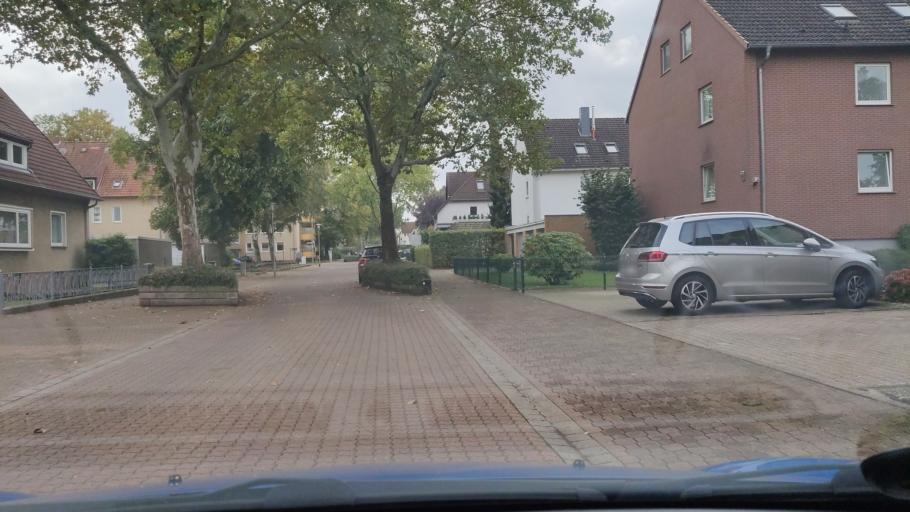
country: DE
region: Lower Saxony
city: Auf der Horst
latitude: 52.4024
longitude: 9.6420
